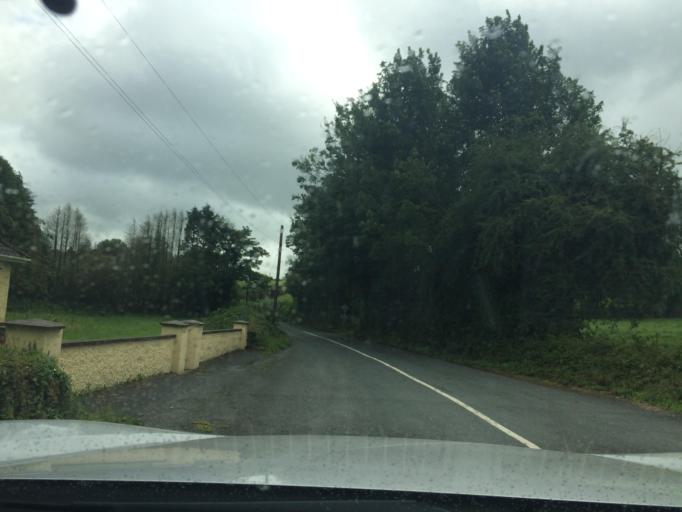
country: IE
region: Munster
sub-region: South Tipperary
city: Cluain Meala
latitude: 52.2117
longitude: -7.7337
